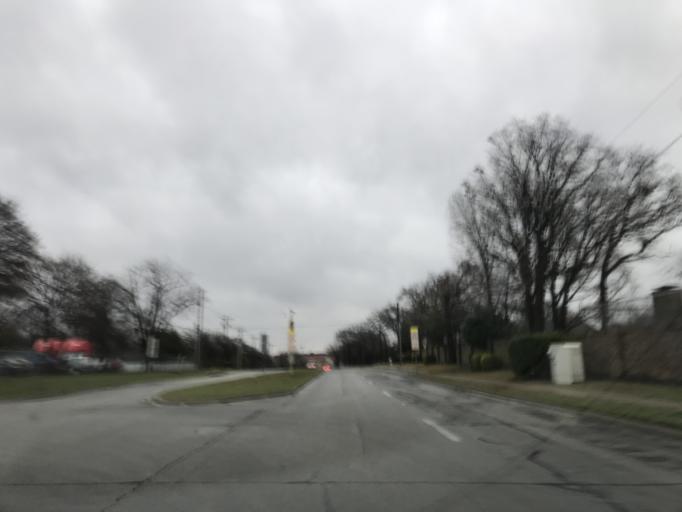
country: US
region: Texas
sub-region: Dallas County
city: Grand Prairie
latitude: 32.7714
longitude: -97.0490
